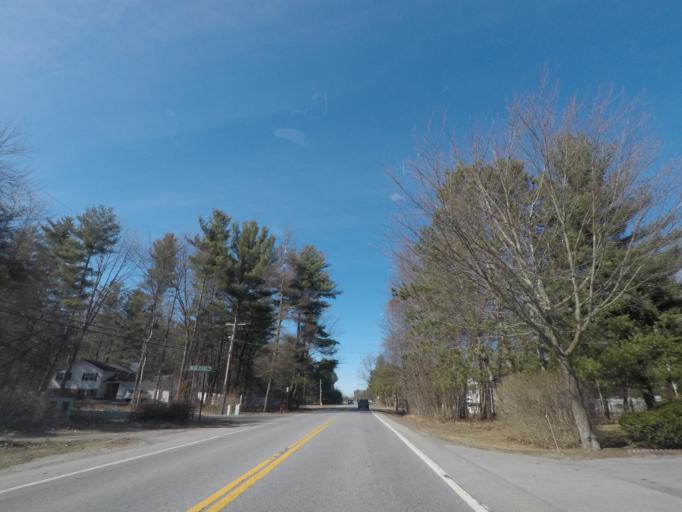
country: US
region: New York
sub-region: Saratoga County
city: Milton
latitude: 43.0372
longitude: -73.8494
